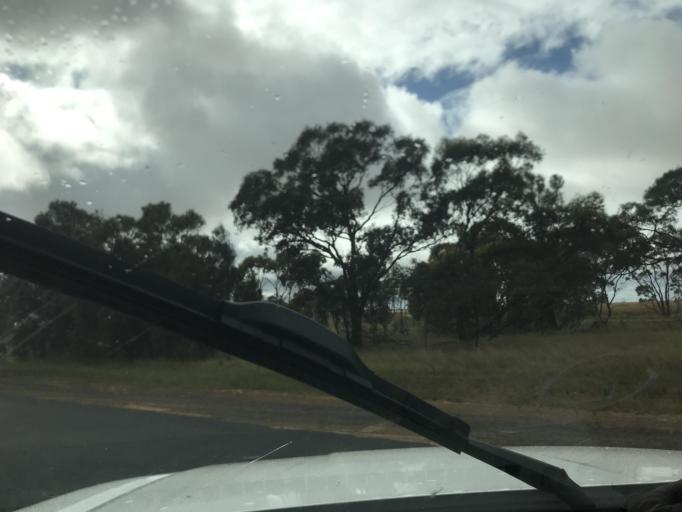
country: AU
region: South Australia
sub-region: Tatiara
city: Bordertown
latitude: -36.3617
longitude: 141.2636
